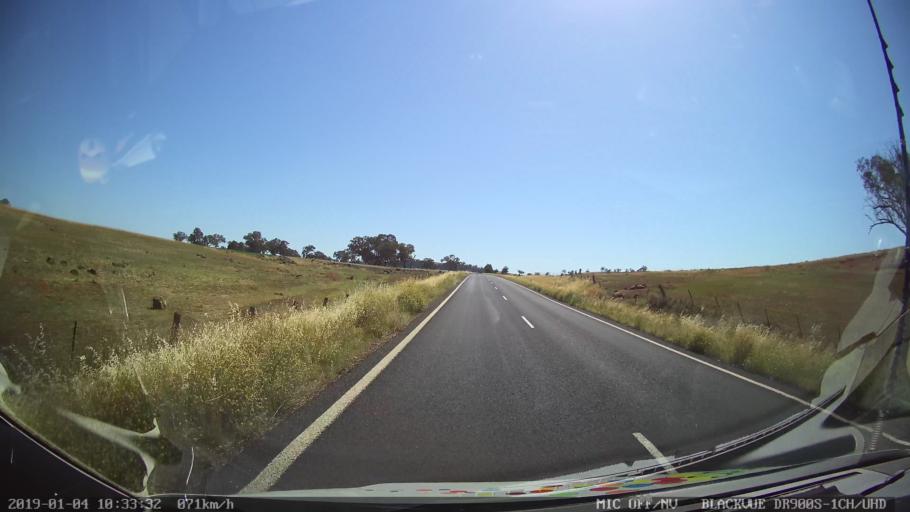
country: AU
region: New South Wales
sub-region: Cabonne
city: Canowindra
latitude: -33.3189
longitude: 148.6506
